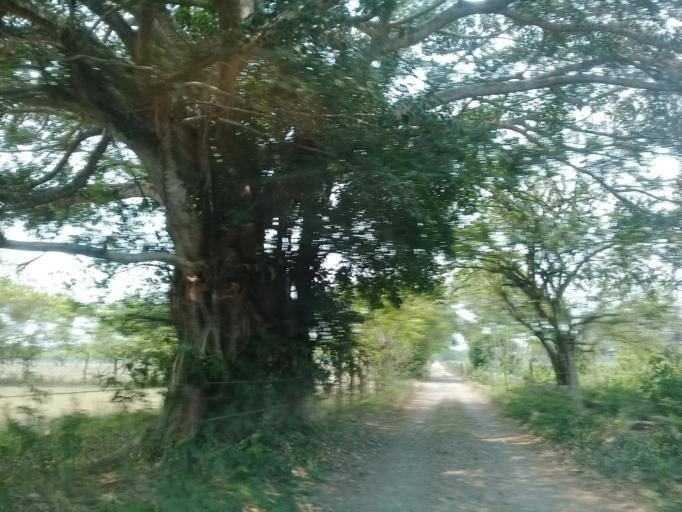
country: MX
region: Veracruz
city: Jamapa
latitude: 18.9263
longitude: -96.2023
